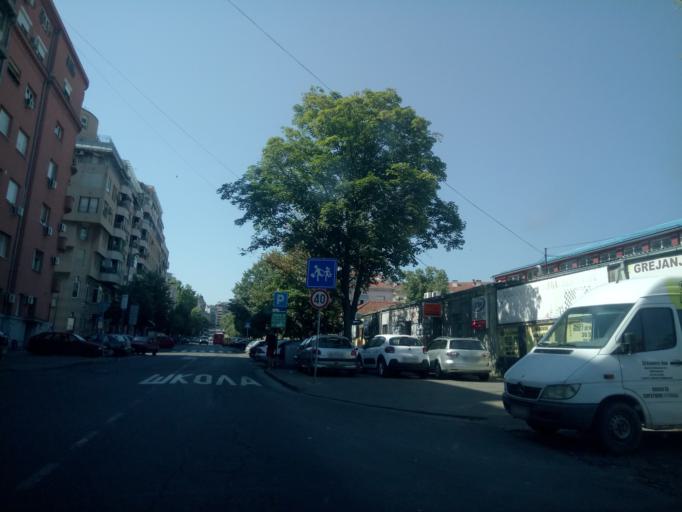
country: RS
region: Central Serbia
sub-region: Belgrade
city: Stari Grad
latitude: 44.8278
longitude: 20.4562
